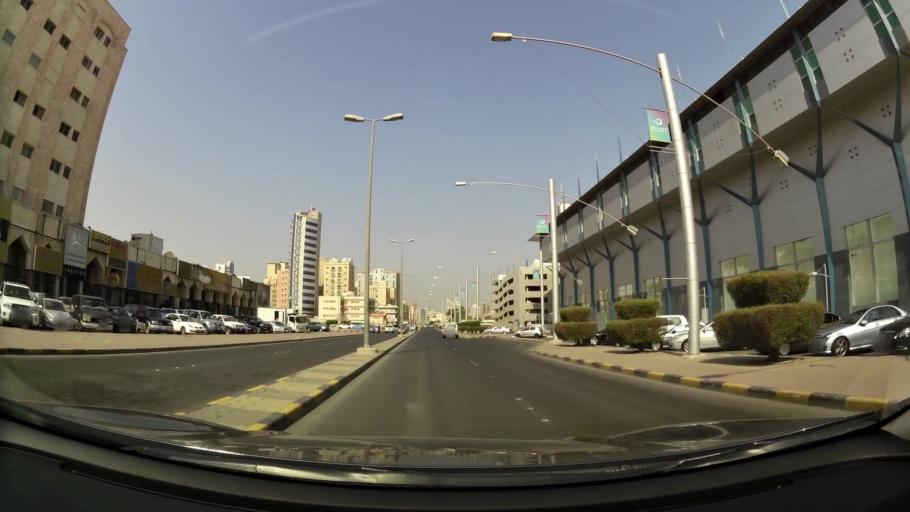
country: KW
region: Muhafazat Hawalli
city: Hawalli
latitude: 29.3403
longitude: 48.0258
